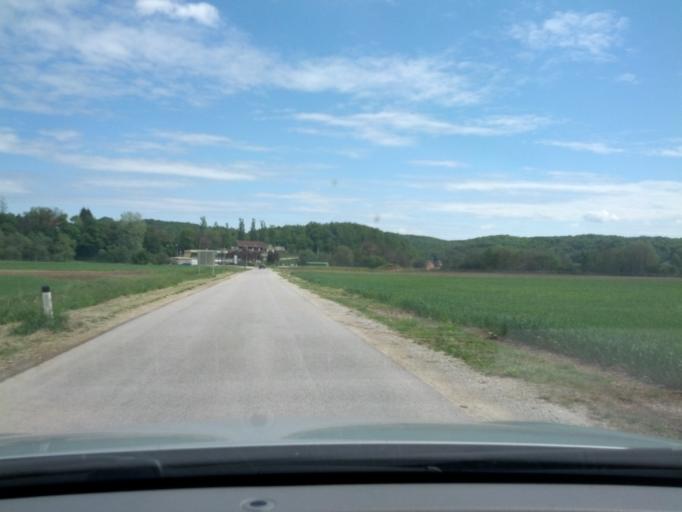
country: SI
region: Podcetrtek
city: Podcetrtek
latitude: 46.1297
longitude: 15.6071
